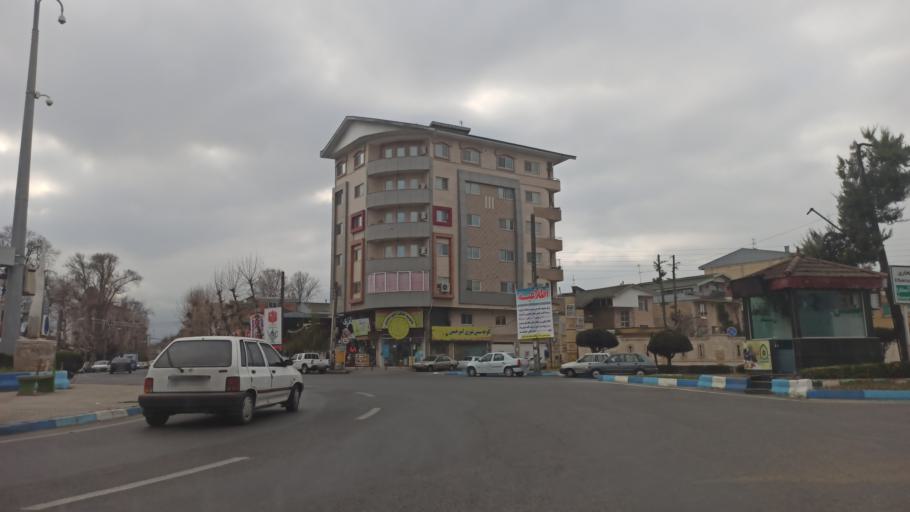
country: IR
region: Gilan
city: Fuman
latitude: 37.2329
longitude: 49.3191
